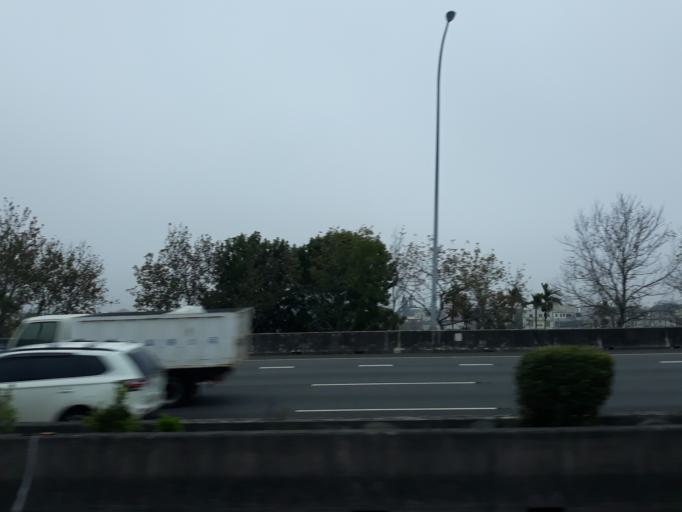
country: TW
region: Taiwan
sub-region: Miaoli
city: Miaoli
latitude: 24.5266
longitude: 120.8238
